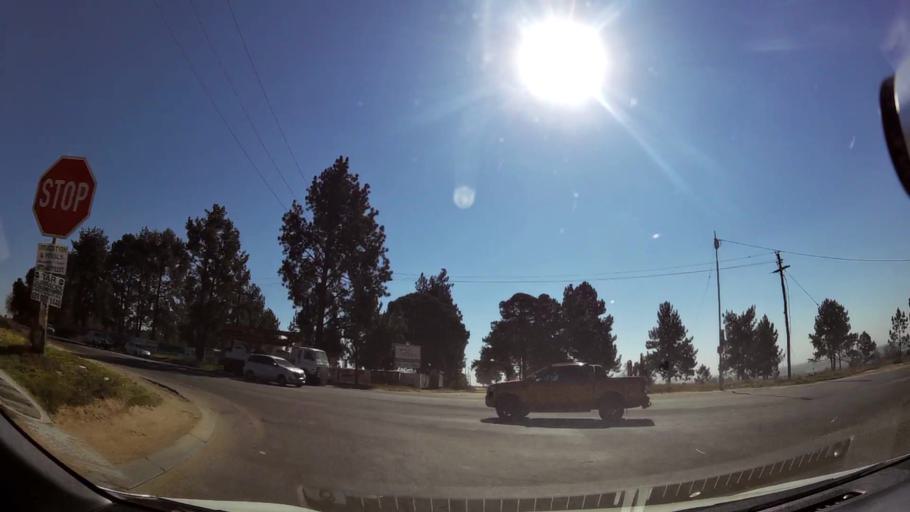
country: ZA
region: Gauteng
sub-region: City of Johannesburg Metropolitan Municipality
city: Midrand
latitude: -25.9409
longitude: 28.0997
